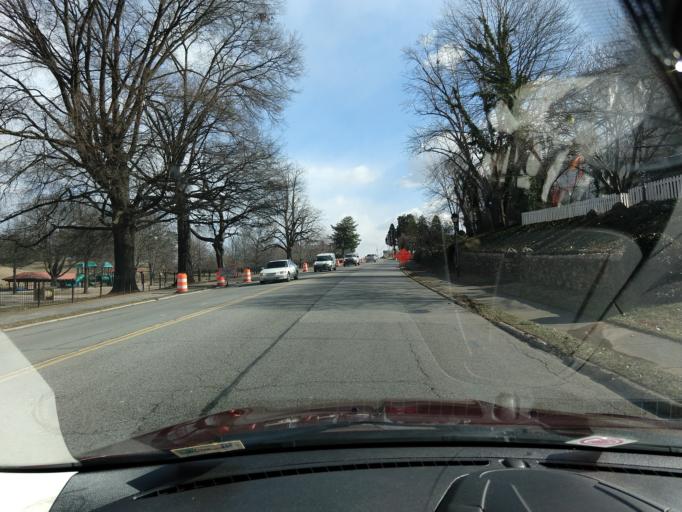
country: US
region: Virginia
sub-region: City of Salem
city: Salem
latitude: 37.2941
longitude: -80.0506
